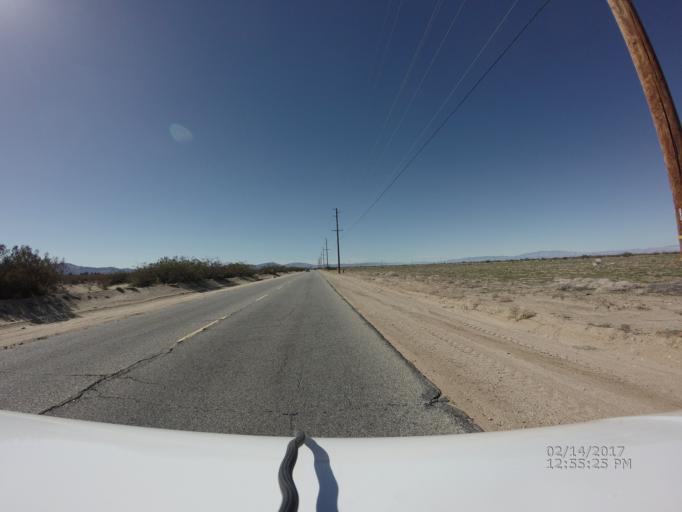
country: US
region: California
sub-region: Los Angeles County
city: Littlerock
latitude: 34.5799
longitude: -117.9267
